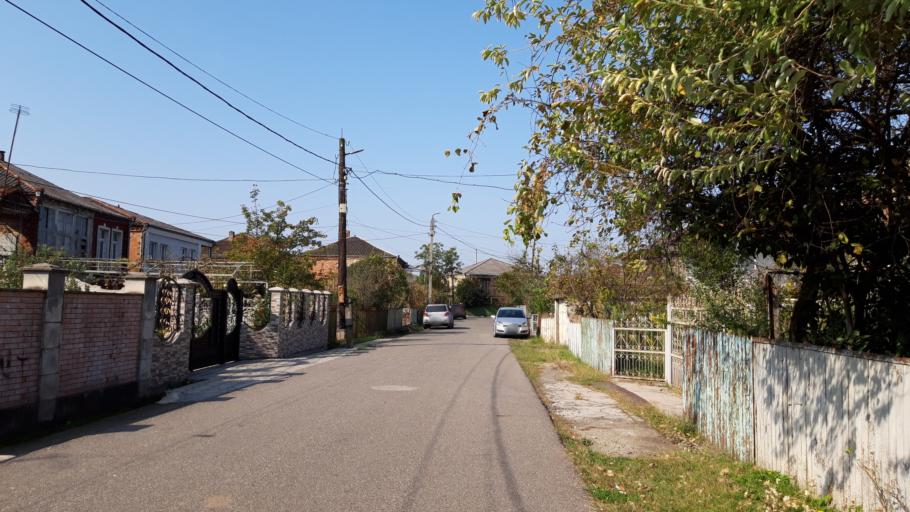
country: GE
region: Imereti
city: Samtredia
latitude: 42.1613
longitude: 42.3355
